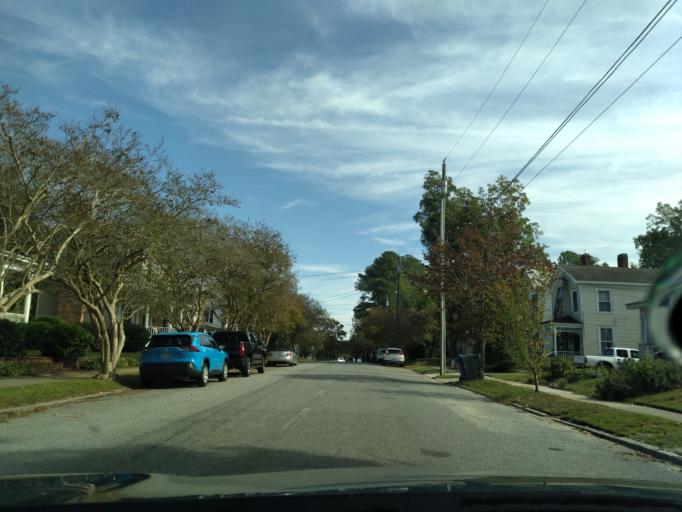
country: US
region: North Carolina
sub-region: Beaufort County
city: Washington
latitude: 35.5381
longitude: -77.0462
